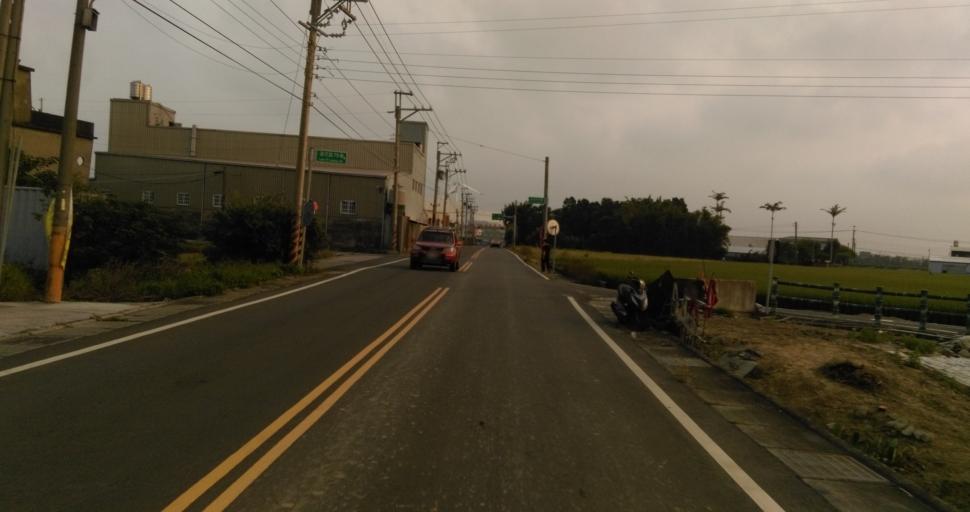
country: TW
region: Taiwan
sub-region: Hsinchu
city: Zhubei
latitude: 24.8639
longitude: 120.9603
